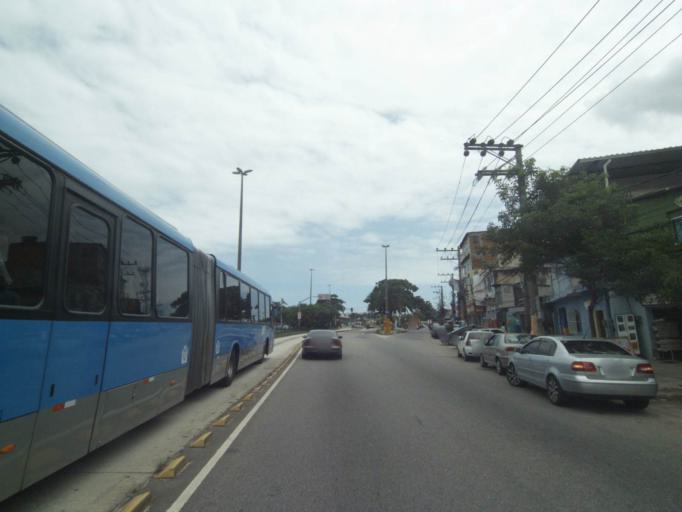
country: BR
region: Rio de Janeiro
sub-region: Sao Joao De Meriti
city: Sao Joao de Meriti
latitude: -22.9509
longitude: -43.3736
